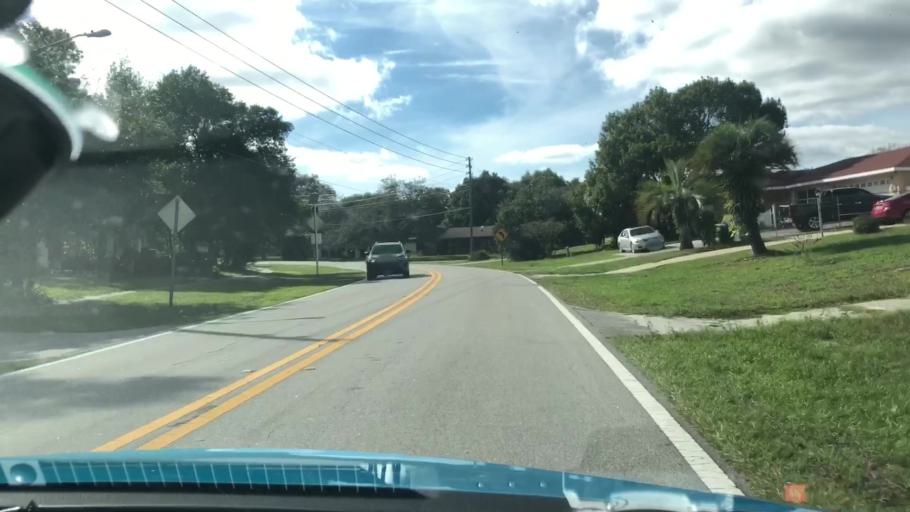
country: US
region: Florida
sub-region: Volusia County
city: Deltona
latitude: 28.9071
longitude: -81.2618
